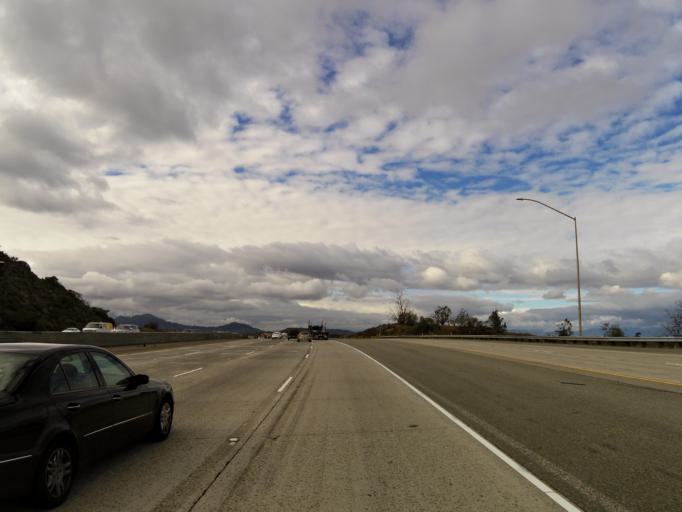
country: US
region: California
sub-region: Ventura County
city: Thousand Oaks
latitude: 34.1749
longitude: -118.8510
